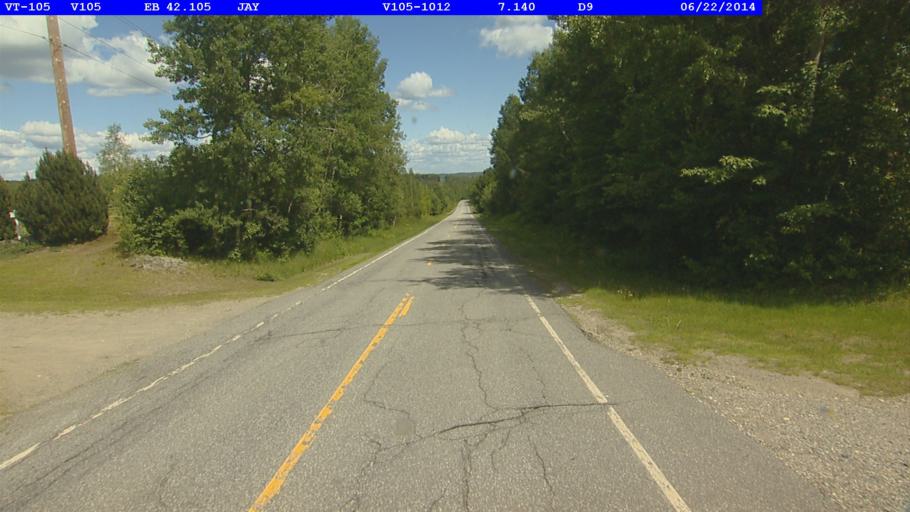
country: CA
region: Quebec
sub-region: Monteregie
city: Sutton
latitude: 44.9692
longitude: -72.4458
